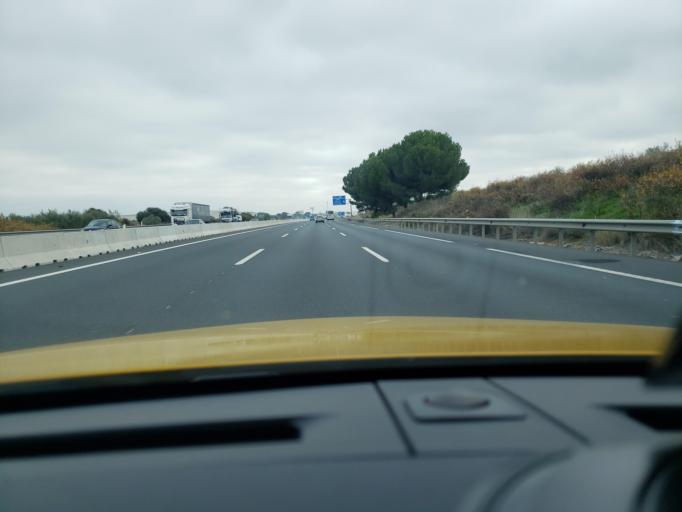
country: ES
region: Andalusia
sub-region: Provincia de Sevilla
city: Umbrete
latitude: 37.3580
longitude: -6.1592
